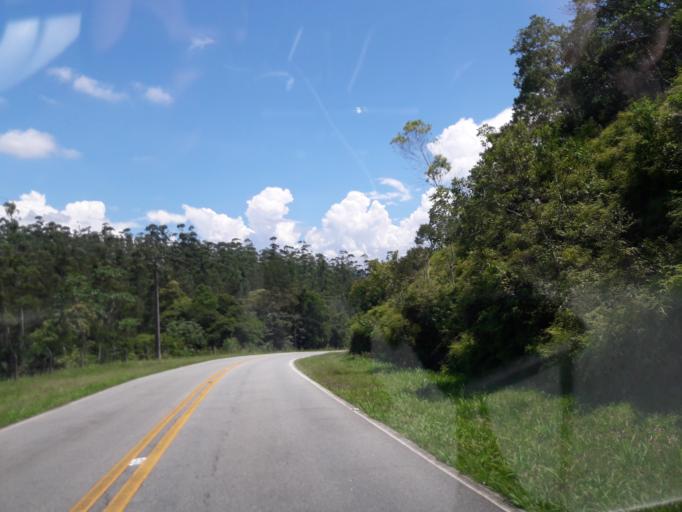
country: BR
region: Parana
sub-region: Antonina
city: Antonina
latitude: -25.5266
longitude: -48.7754
